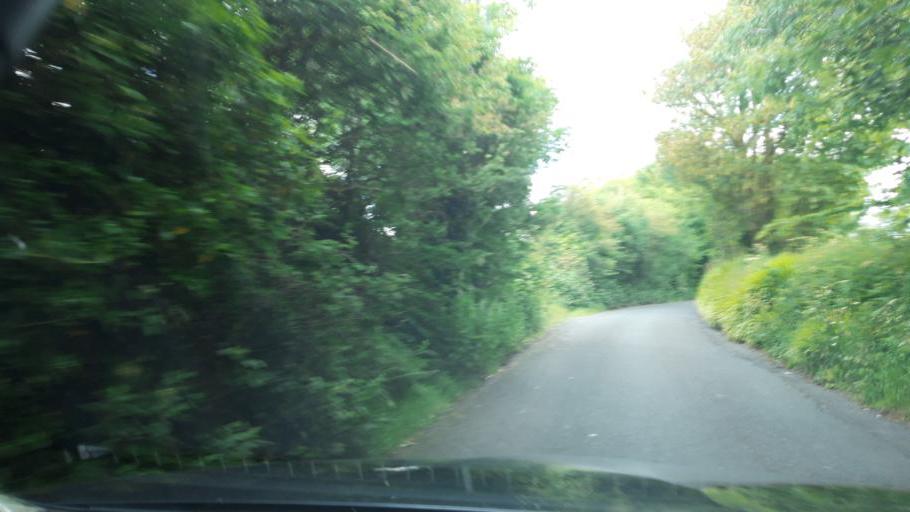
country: IE
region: Leinster
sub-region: Loch Garman
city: Loch Garman
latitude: 52.2866
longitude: -6.5187
